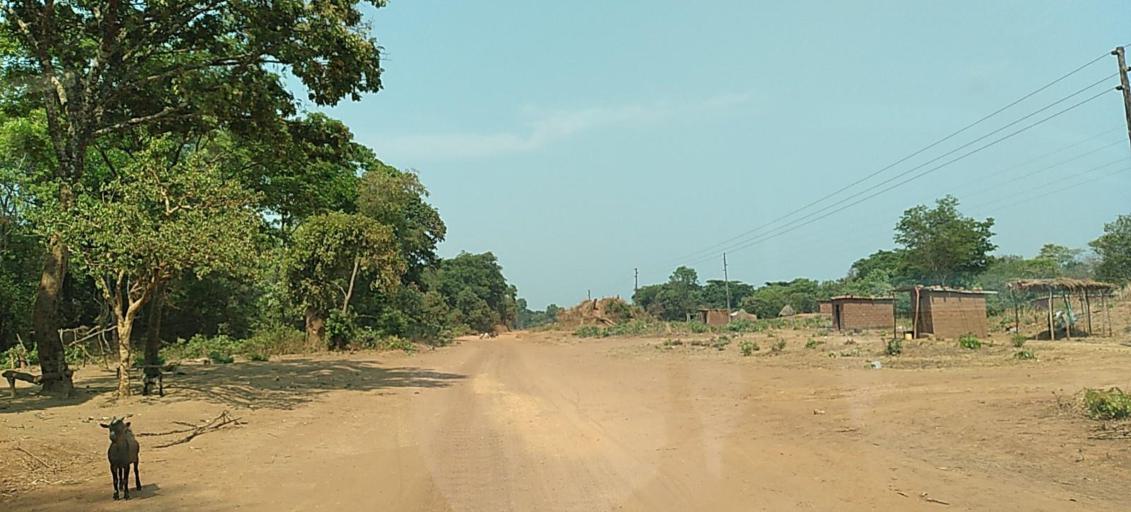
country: ZM
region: Copperbelt
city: Chingola
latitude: -13.0441
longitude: 27.4383
